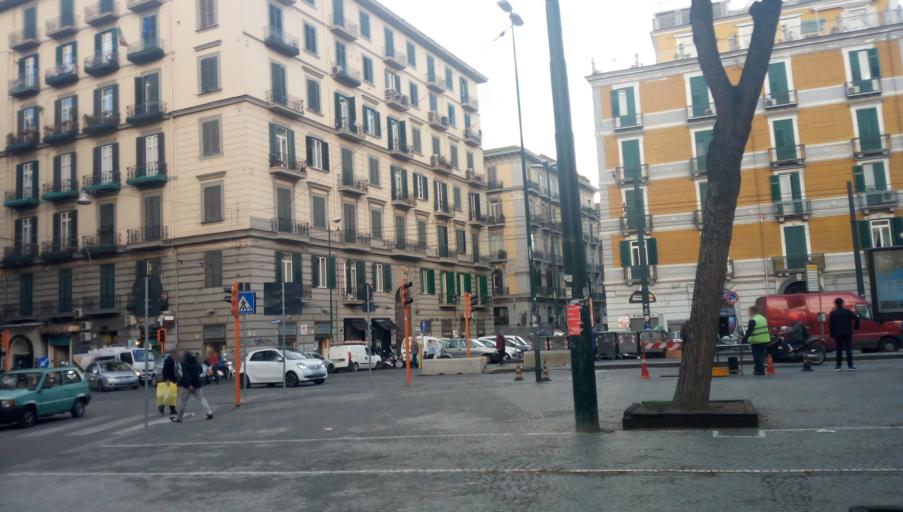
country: IT
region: Campania
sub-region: Provincia di Napoli
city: Napoli
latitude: 40.8539
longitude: 14.2682
